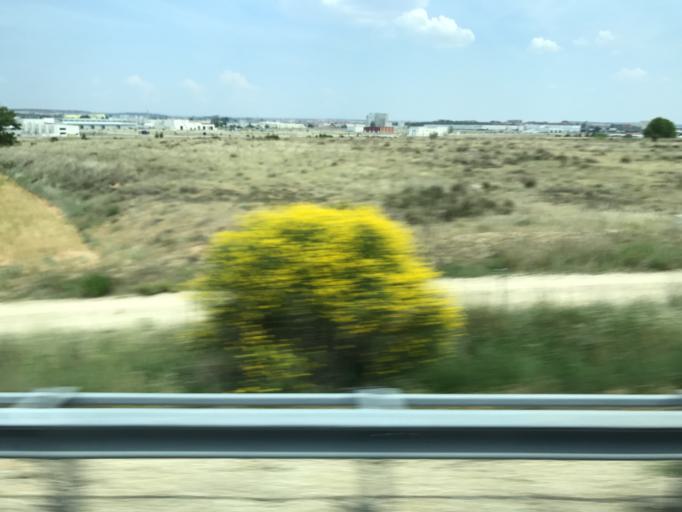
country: ES
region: Castille and Leon
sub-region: Provincia de Burgos
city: Aranda de Duero
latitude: 41.6512
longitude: -3.7216
